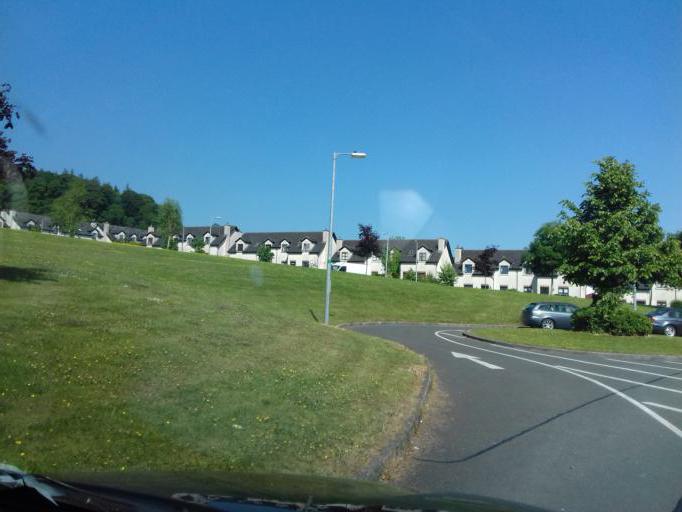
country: IE
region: Leinster
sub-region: An Mhi
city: Slane
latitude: 53.7123
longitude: -6.5533
